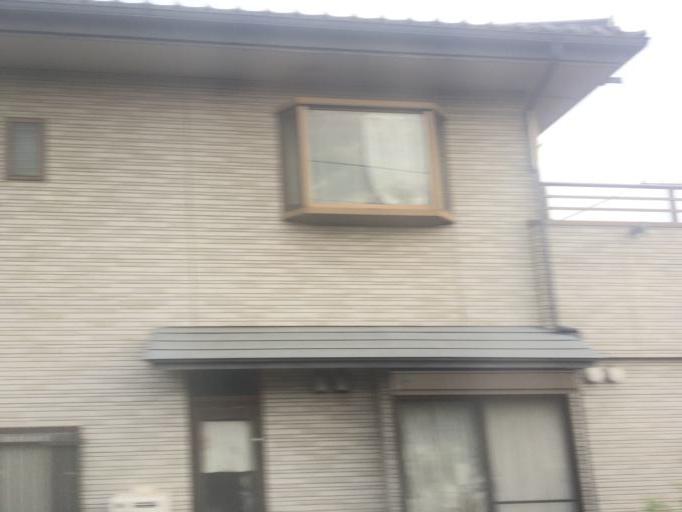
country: JP
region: Tokyo
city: Fussa
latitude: 35.7760
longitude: 139.3460
